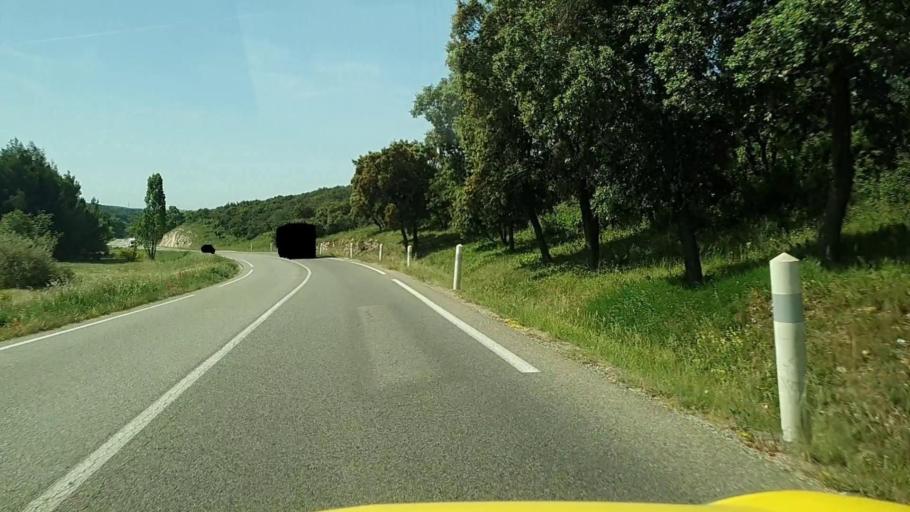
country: FR
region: Languedoc-Roussillon
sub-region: Departement du Gard
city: Connaux
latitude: 44.0322
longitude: 4.5812
